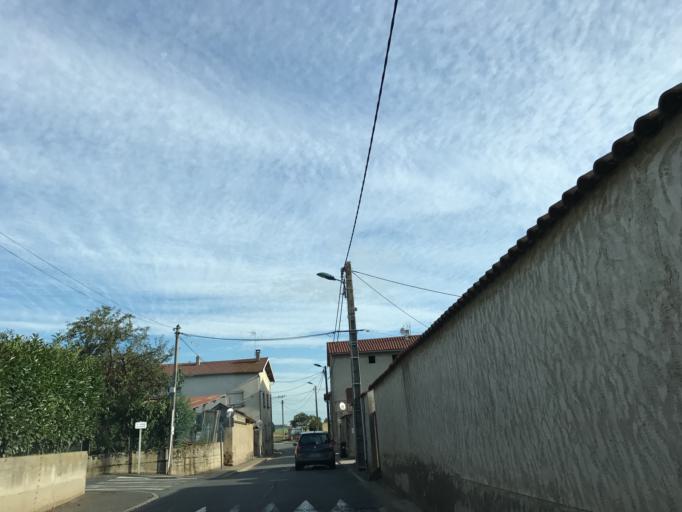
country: FR
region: Rhone-Alpes
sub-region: Departement de l'Ain
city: Miribel
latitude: 45.8318
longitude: 4.9471
